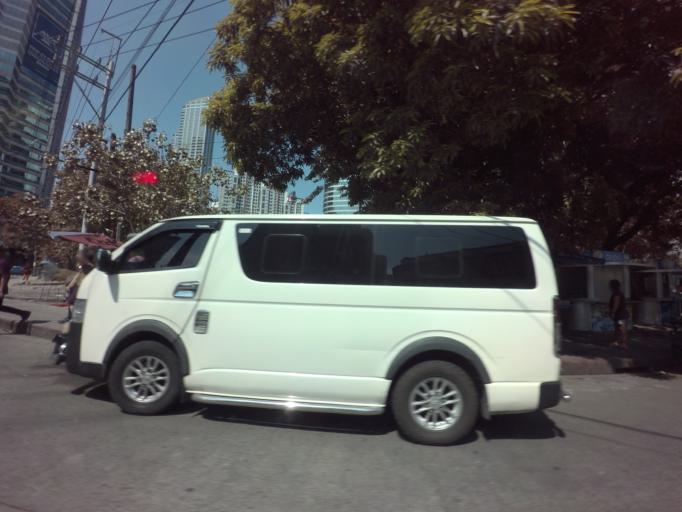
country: PH
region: Metro Manila
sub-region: Makati City
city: Makati City
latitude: 14.5602
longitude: 121.0140
